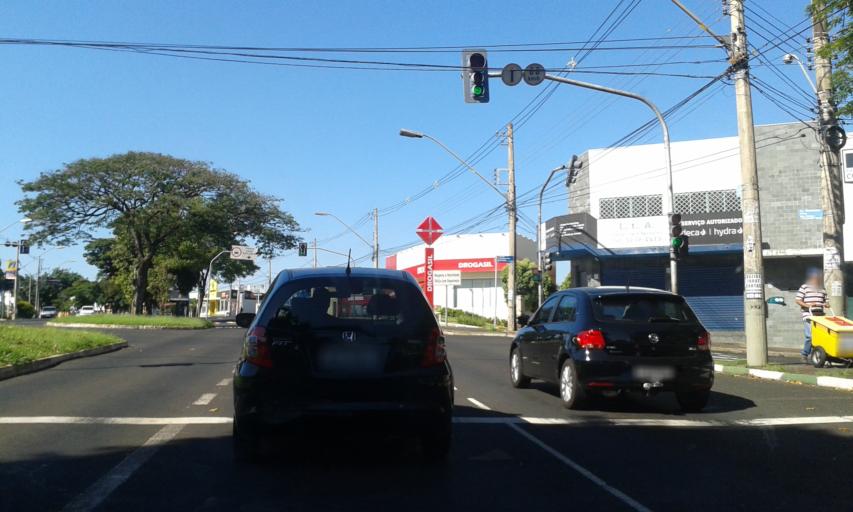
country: BR
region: Minas Gerais
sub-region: Uberlandia
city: Uberlandia
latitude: -18.9213
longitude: -48.2628
